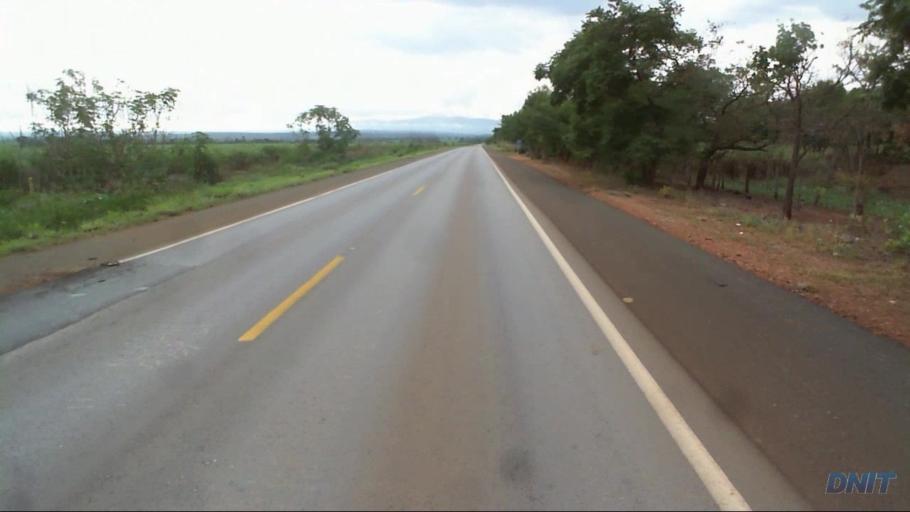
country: BR
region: Goias
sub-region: Uruacu
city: Uruacu
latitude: -14.7152
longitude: -49.1053
